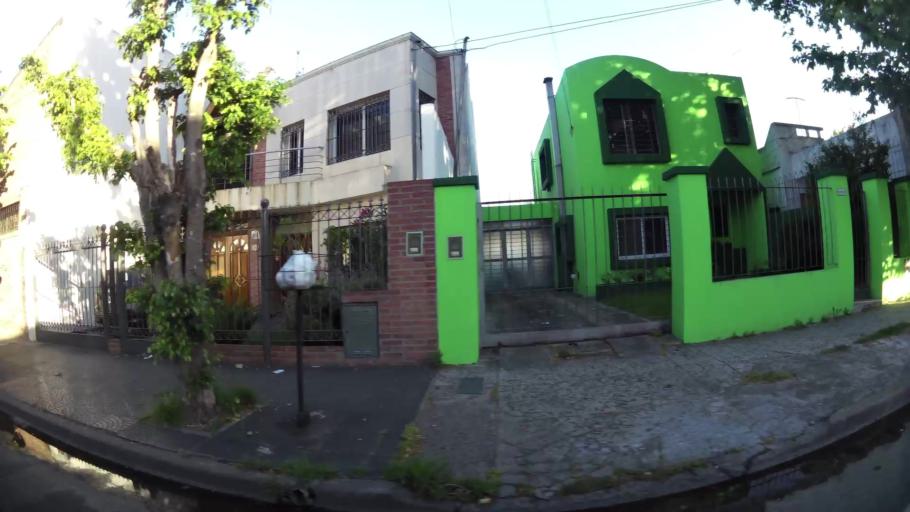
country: AR
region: Buenos Aires
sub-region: Partido de General San Martin
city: General San Martin
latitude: -34.5671
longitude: -58.5456
